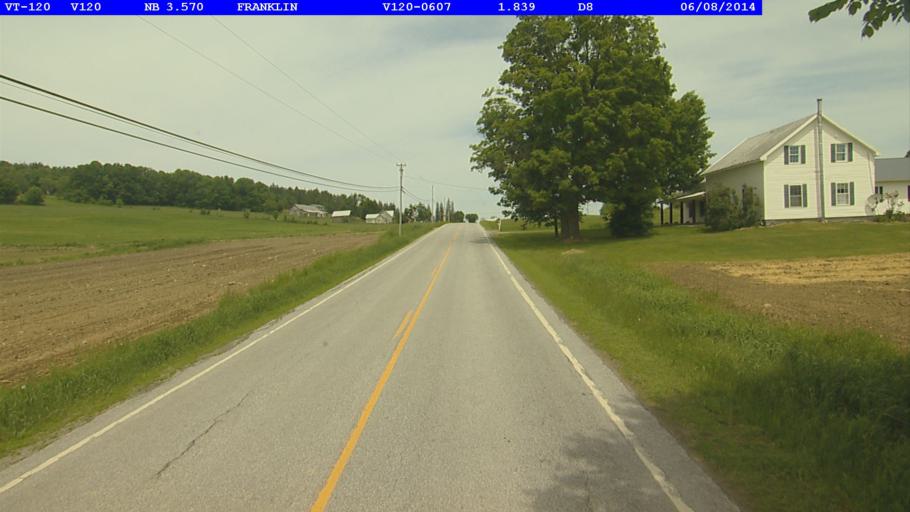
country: US
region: Vermont
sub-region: Franklin County
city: Enosburg Falls
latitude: 44.9593
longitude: -72.9063
